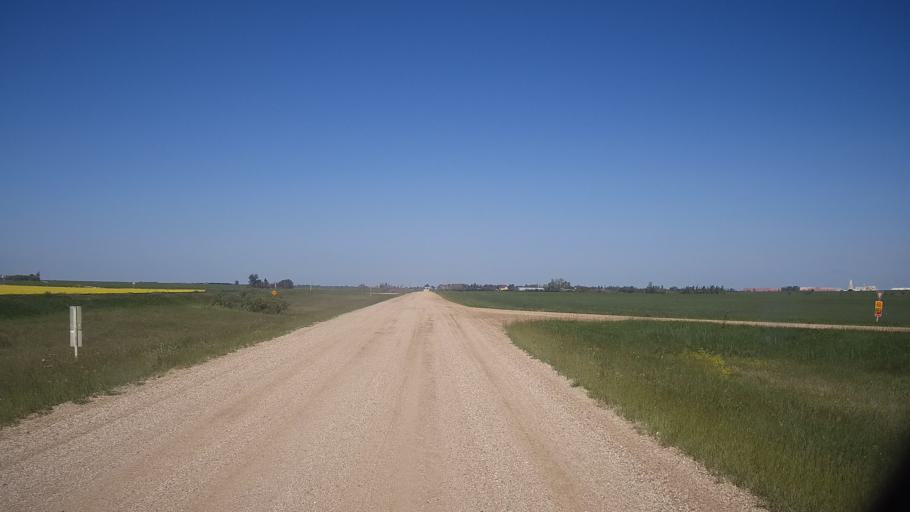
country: CA
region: Saskatchewan
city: Watrous
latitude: 51.8815
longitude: -106.0238
